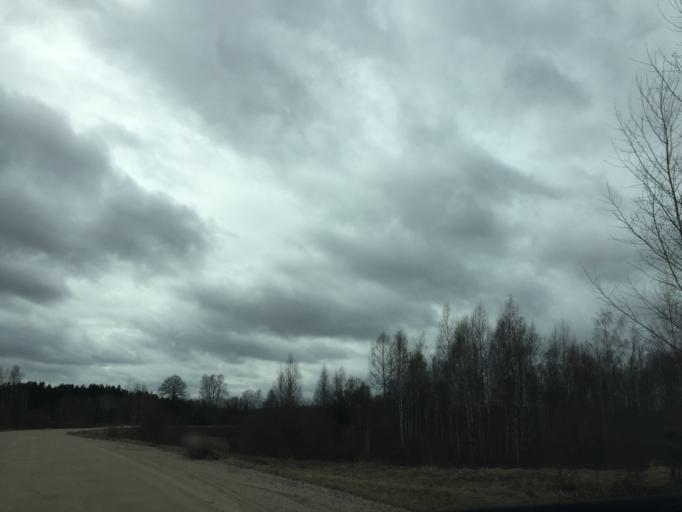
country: LV
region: Kraslavas Rajons
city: Kraslava
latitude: 55.9572
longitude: 27.0365
